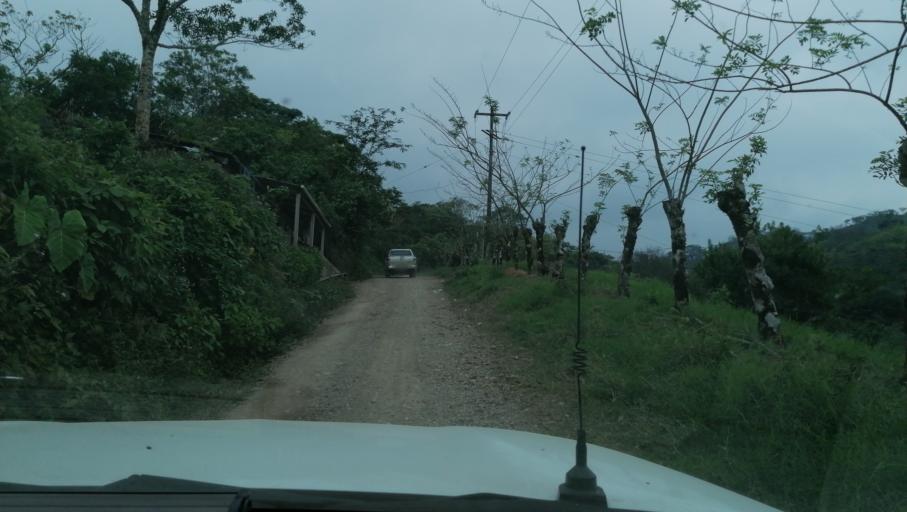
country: MX
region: Chiapas
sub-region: Francisco Leon
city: San Miguel la Sardina
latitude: 17.3275
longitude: -93.3109
